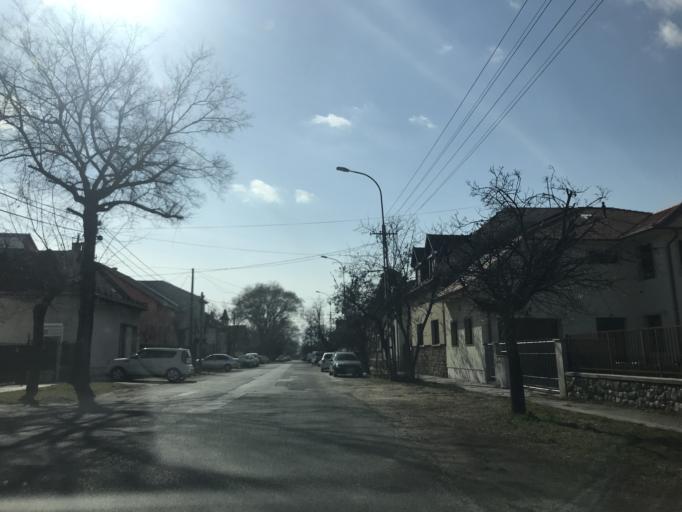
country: HU
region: Budapest
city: Budapest XIV. keruelet
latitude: 47.5386
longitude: 19.1203
